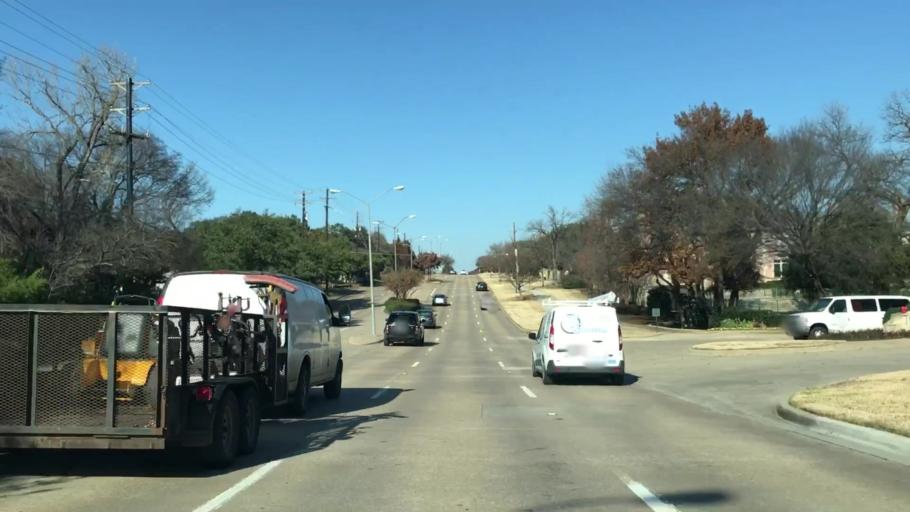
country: US
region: Texas
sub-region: Dallas County
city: University Park
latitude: 32.9112
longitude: -96.7864
